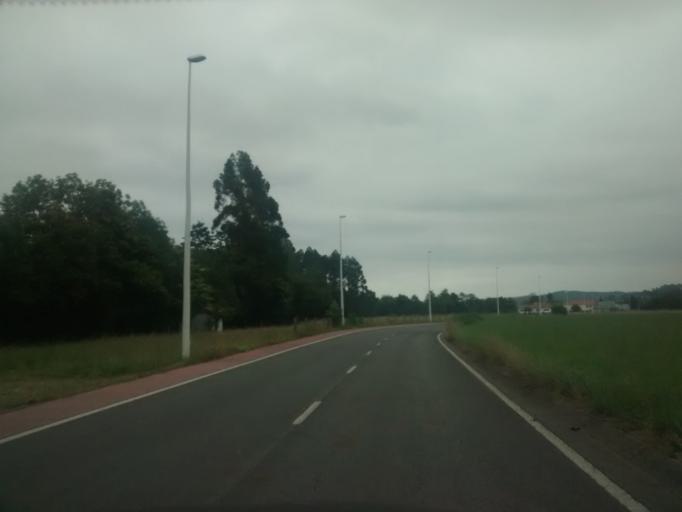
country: ES
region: Cantabria
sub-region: Provincia de Cantabria
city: Cabezon de la Sal
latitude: 43.2865
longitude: -4.2326
